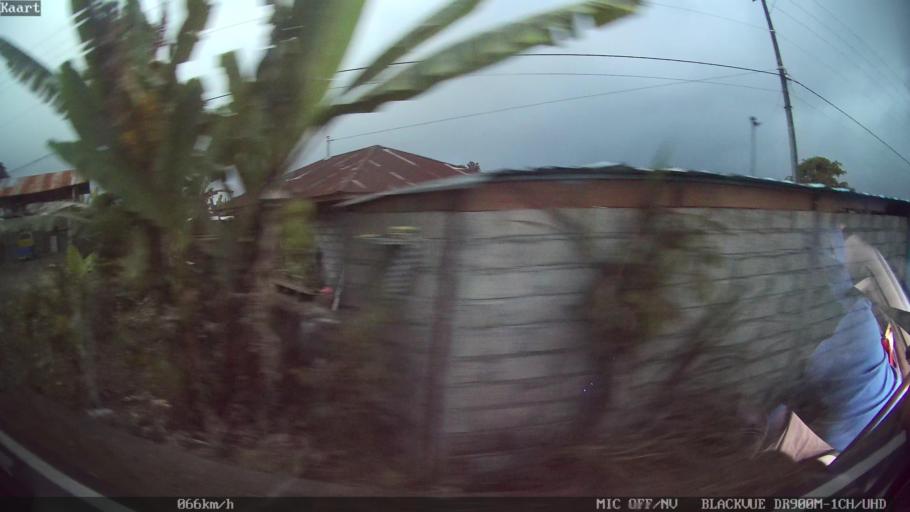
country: ID
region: Bali
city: Banjar Kedisan
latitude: -8.2764
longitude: 115.3261
